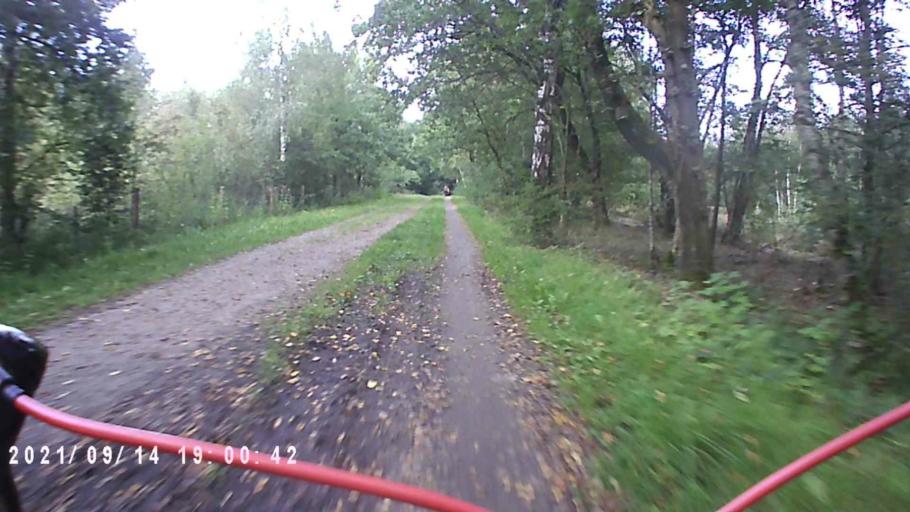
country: NL
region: Drenthe
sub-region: Gemeente Aa en Hunze
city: Anloo
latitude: 53.0345
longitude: 6.7254
